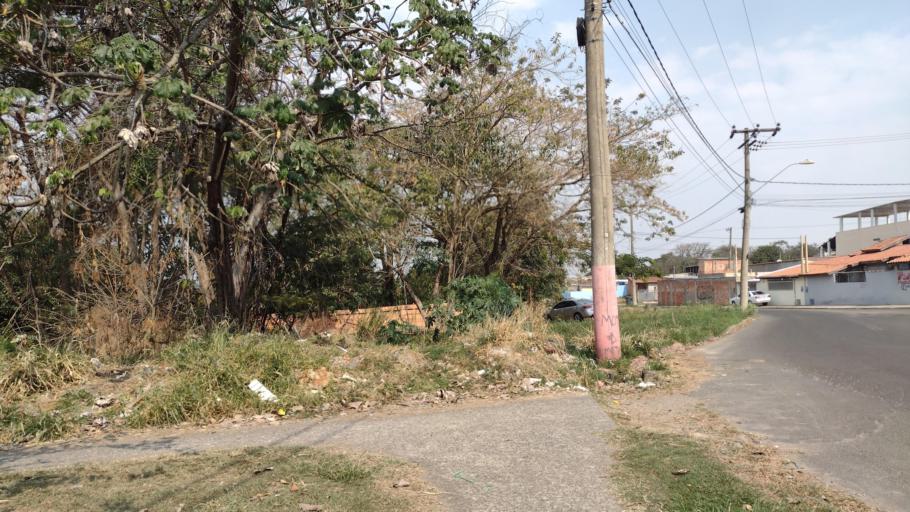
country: BR
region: Sao Paulo
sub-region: Sorocaba
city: Sorocaba
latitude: -23.4343
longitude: -47.4618
